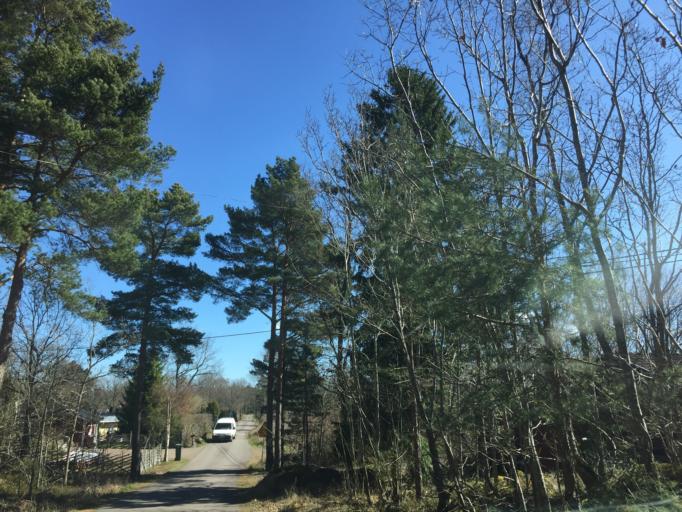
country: SE
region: Kalmar
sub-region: Oskarshamns Kommun
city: Oskarshamn
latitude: 57.2317
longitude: 16.4843
